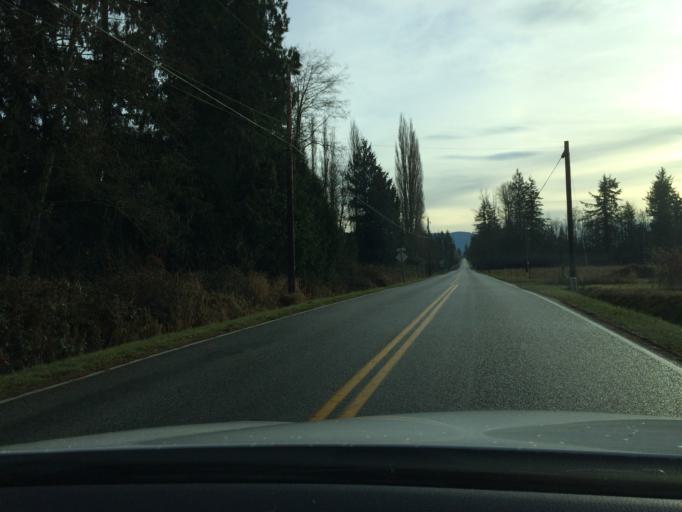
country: US
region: Washington
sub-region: Whatcom County
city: Nooksack
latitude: 48.9018
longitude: -122.2875
